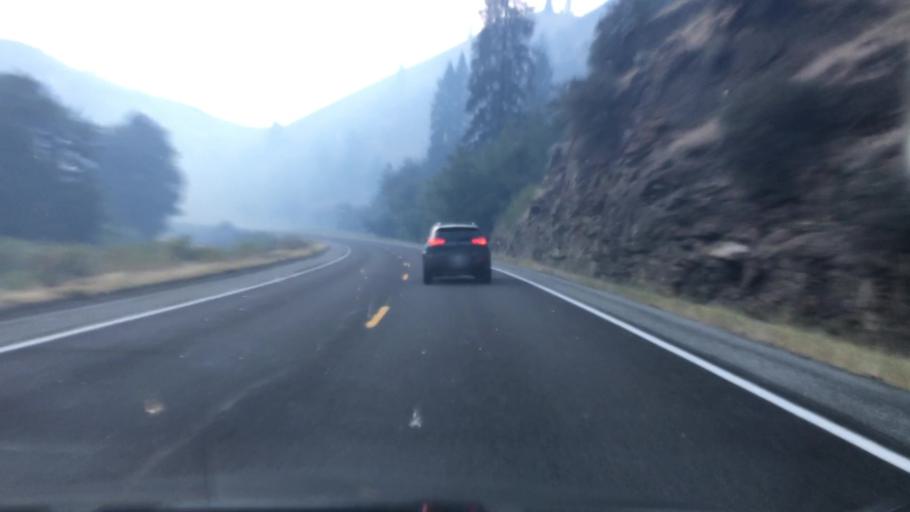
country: US
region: Idaho
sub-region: Valley County
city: McCall
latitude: 45.2812
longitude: -116.3463
